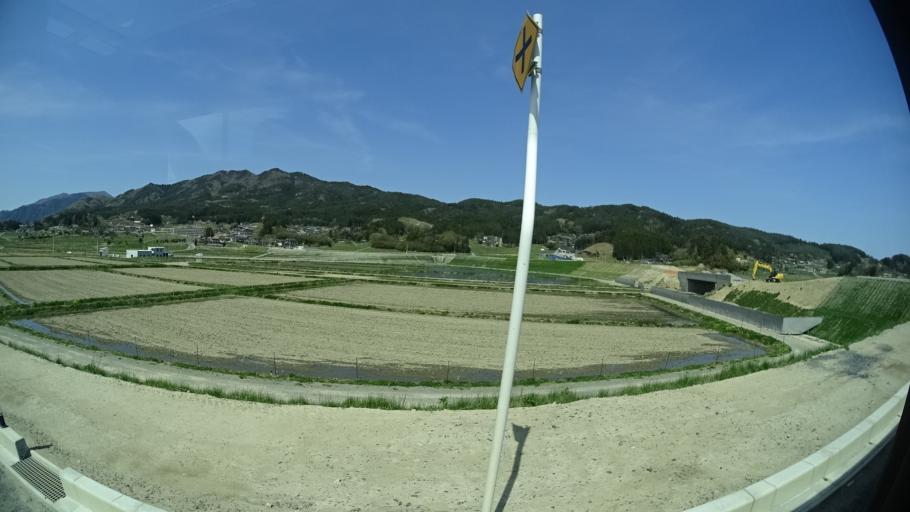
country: JP
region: Iwate
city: Ofunato
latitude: 38.9941
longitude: 141.6906
